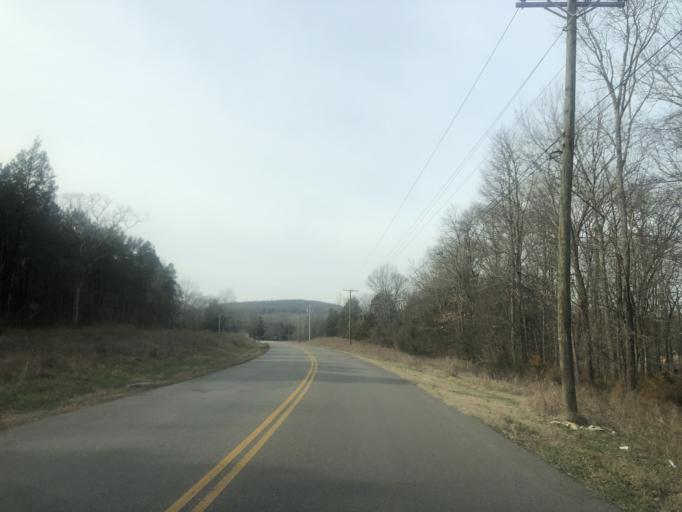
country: US
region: Tennessee
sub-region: Williamson County
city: Nolensville
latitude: 35.8623
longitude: -86.5756
